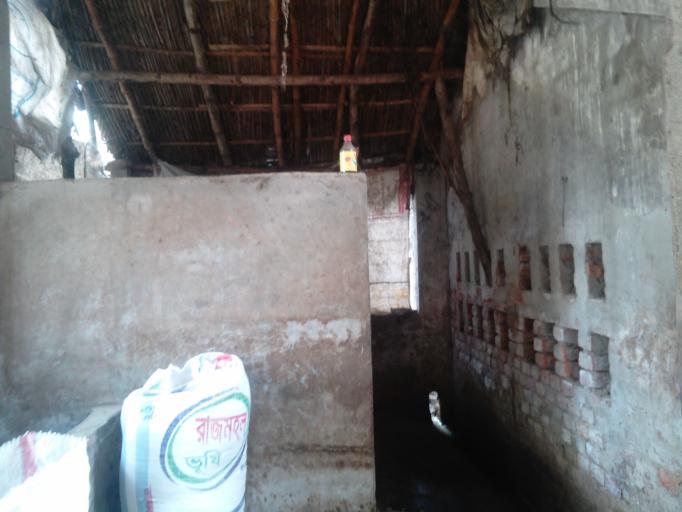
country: BD
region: Khulna
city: Kesabpur
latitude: 22.7996
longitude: 89.2623
